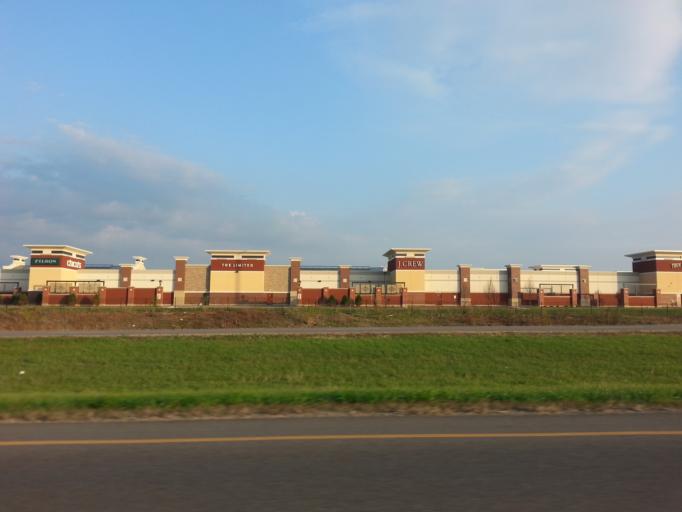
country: US
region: Minnesota
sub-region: Dakota County
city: Eagan
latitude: 44.8173
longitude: -93.2151
